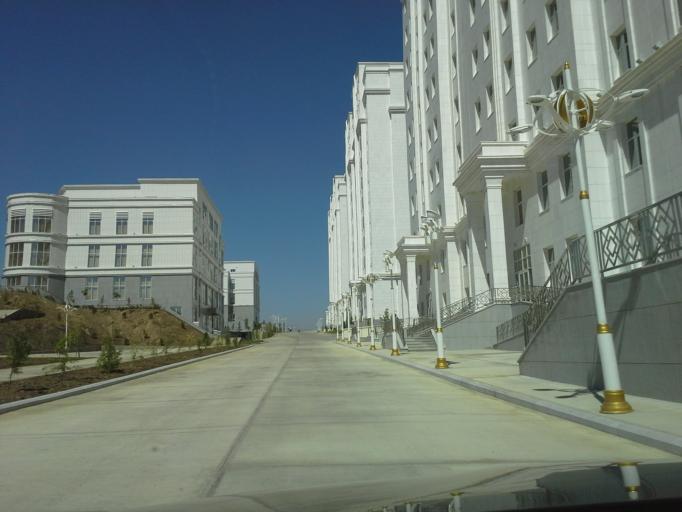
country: TM
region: Ahal
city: Ashgabat
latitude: 37.9421
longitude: 58.3495
